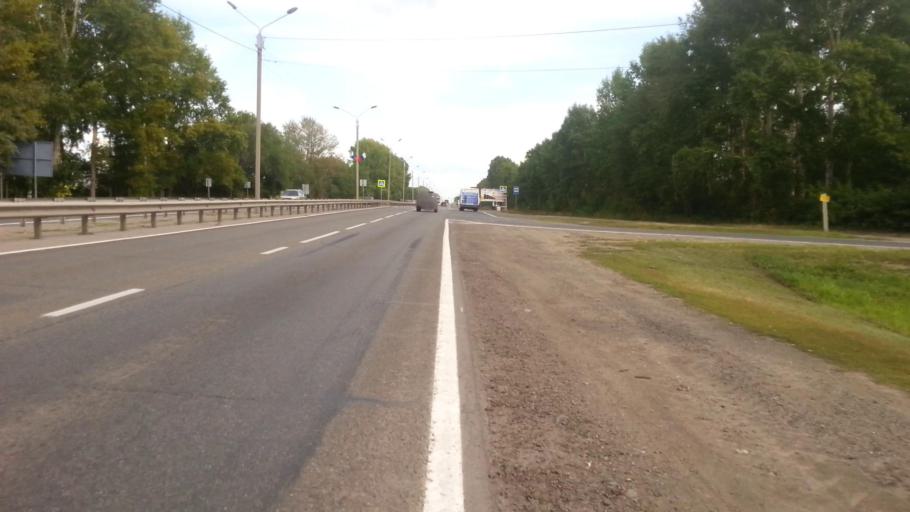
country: RU
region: Altai Krai
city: Vlasikha
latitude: 53.3533
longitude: 83.5567
